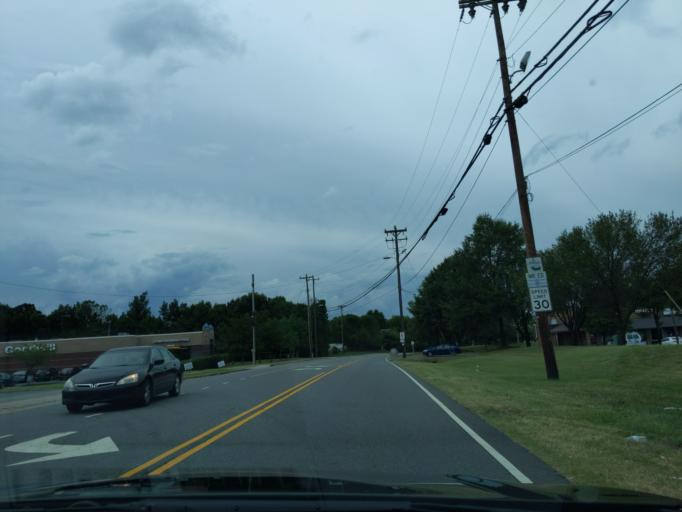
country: US
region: North Carolina
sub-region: Cabarrus County
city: Harrisburg
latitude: 35.3145
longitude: -80.7009
